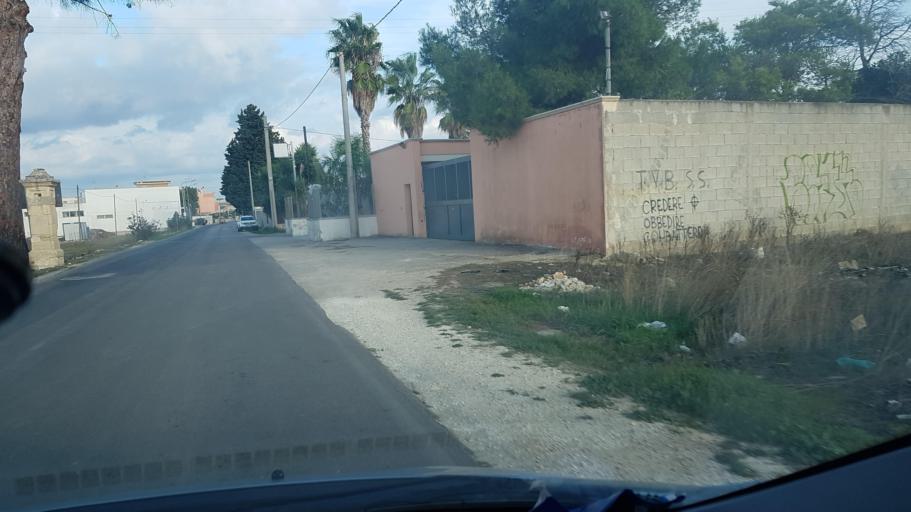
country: IT
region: Apulia
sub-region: Provincia di Lecce
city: Carmiano
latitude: 40.3457
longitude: 18.0307
